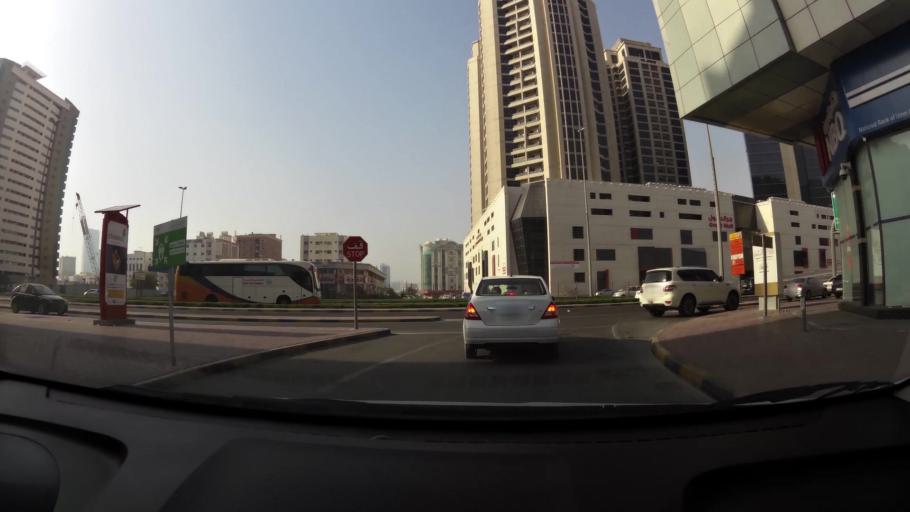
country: AE
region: Ajman
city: Ajman
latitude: 25.3917
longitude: 55.4381
